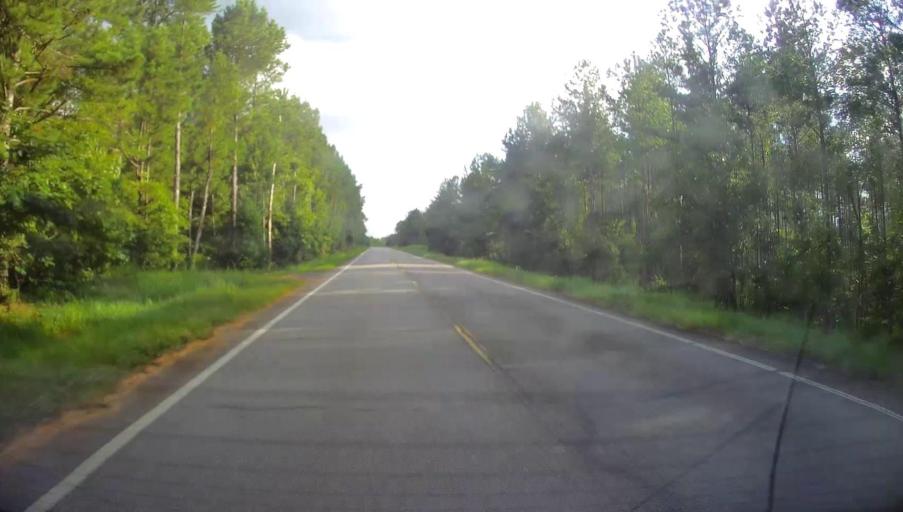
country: US
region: Georgia
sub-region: Crawford County
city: Roberta
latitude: 32.8216
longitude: -84.0215
